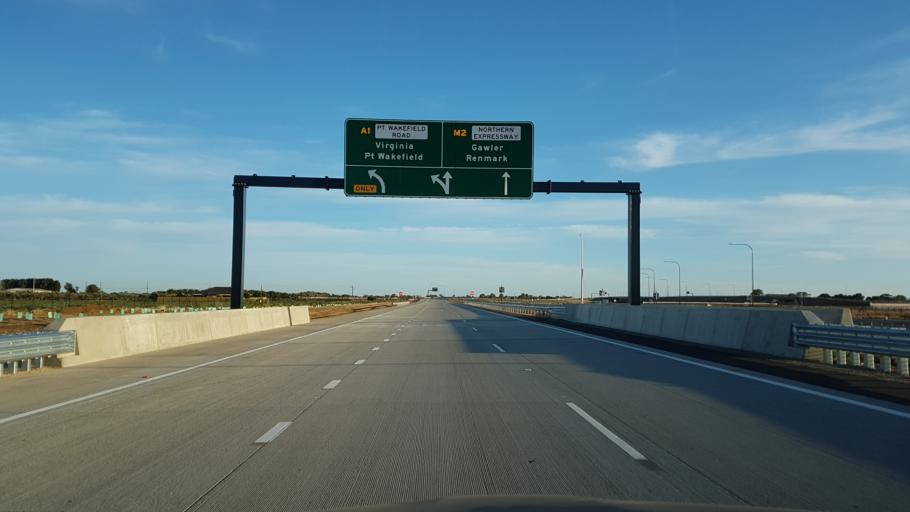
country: AU
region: South Australia
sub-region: Playford
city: Virginia
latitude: -34.7161
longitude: 138.5720
